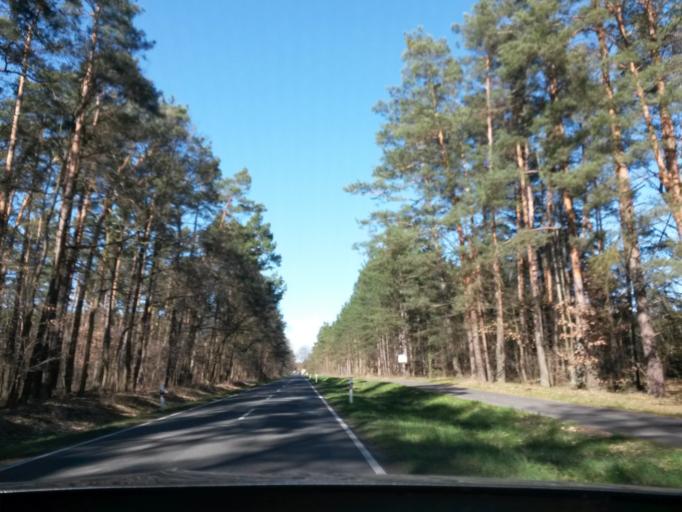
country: DE
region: Brandenburg
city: Rehfelde
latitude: 52.4745
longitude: 13.9090
